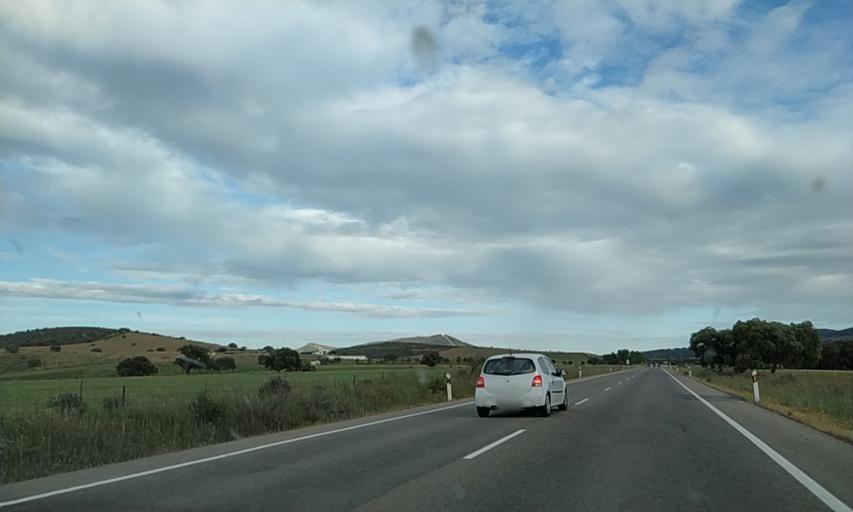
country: ES
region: Extremadura
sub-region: Provincia de Caceres
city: Pedroso de Acim
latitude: 39.8544
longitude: -6.4216
